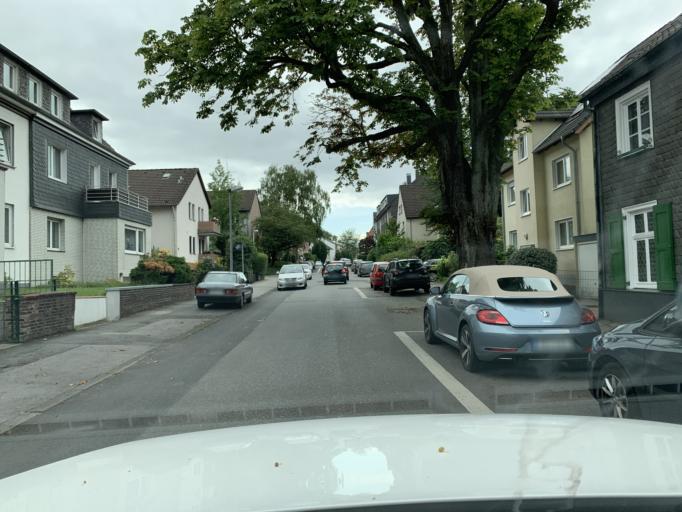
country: DE
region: North Rhine-Westphalia
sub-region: Regierungsbezirk Dusseldorf
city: Muelheim (Ruhr)
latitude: 51.4453
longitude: 6.9022
